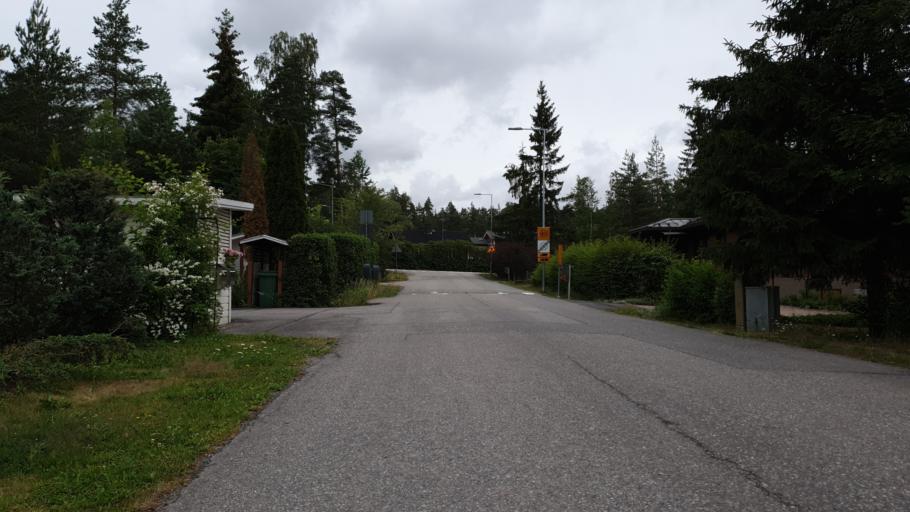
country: FI
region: Uusimaa
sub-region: Helsinki
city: Teekkarikylae
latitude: 60.2853
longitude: 24.9031
